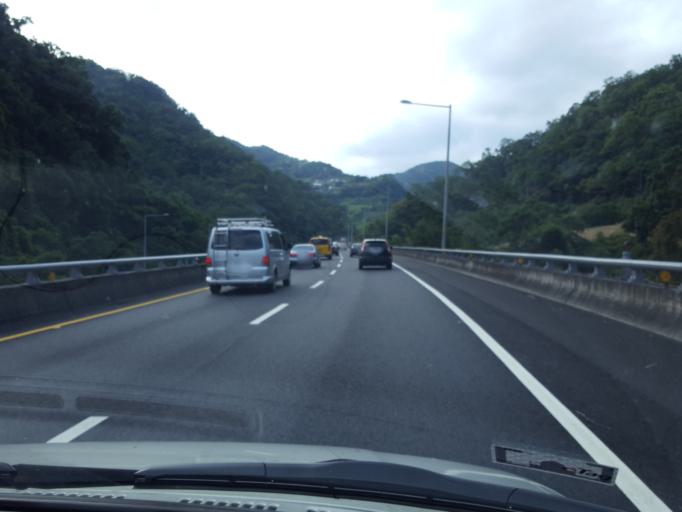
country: TW
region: Taiwan
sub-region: Keelung
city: Keelung
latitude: 24.9461
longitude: 121.7089
